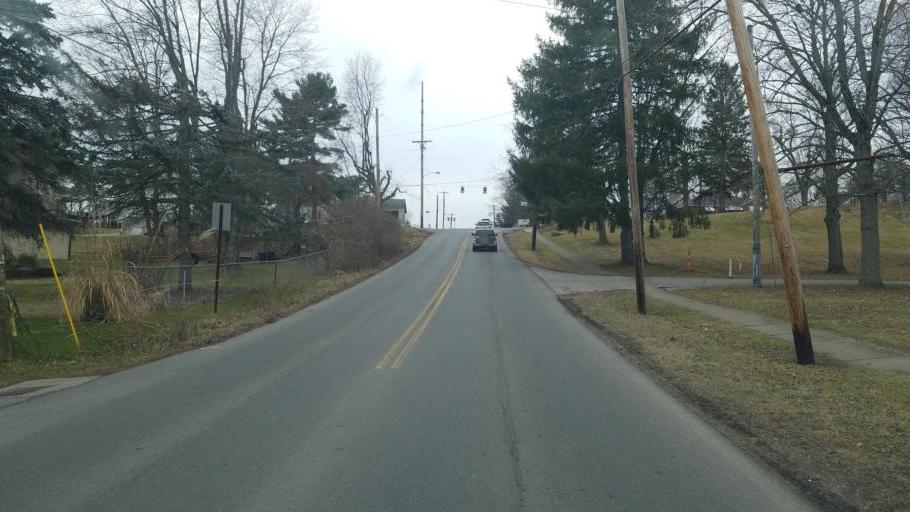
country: US
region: Ohio
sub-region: Richland County
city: Lincoln Heights
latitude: 40.7702
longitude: -82.4961
